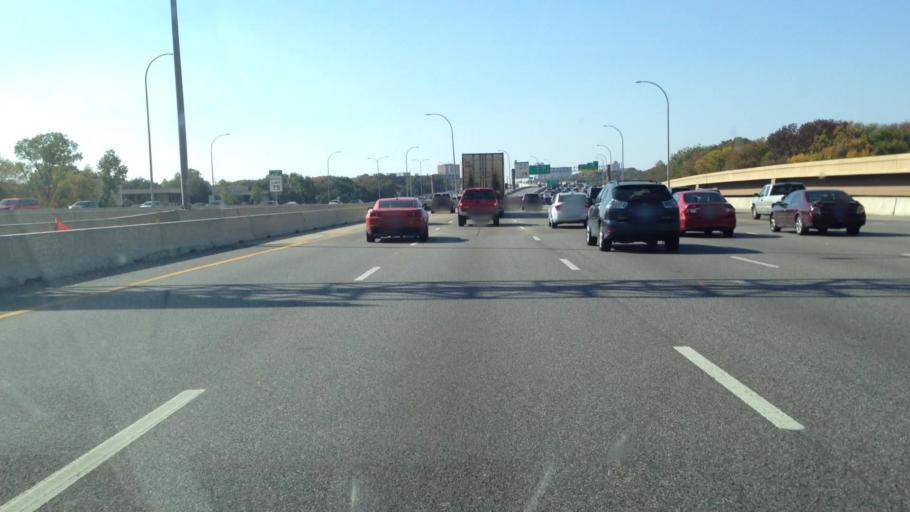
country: US
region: Texas
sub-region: Dallas County
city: Richardson
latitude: 32.9243
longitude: -96.7802
